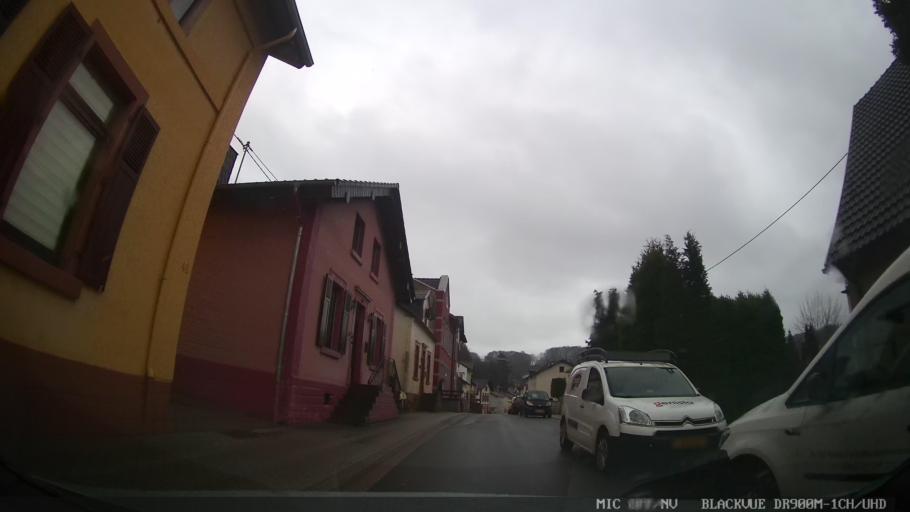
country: DE
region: Saarland
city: Mettlach
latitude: 49.4963
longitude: 6.6024
